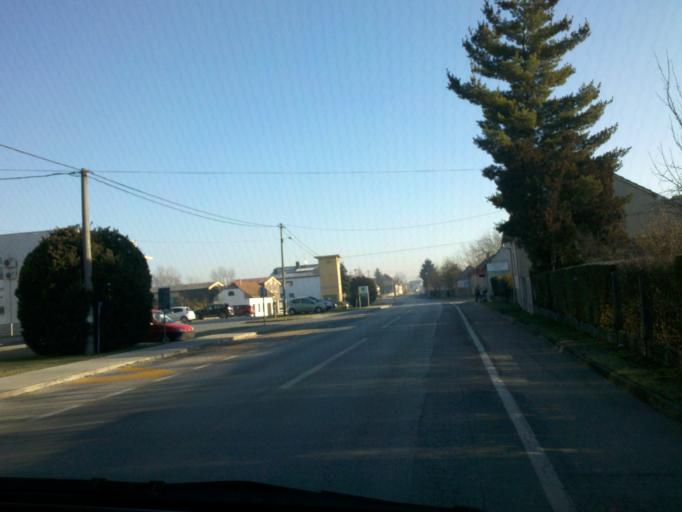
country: HR
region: Medimurska
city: Mala Subotica
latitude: 46.3755
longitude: 16.5282
